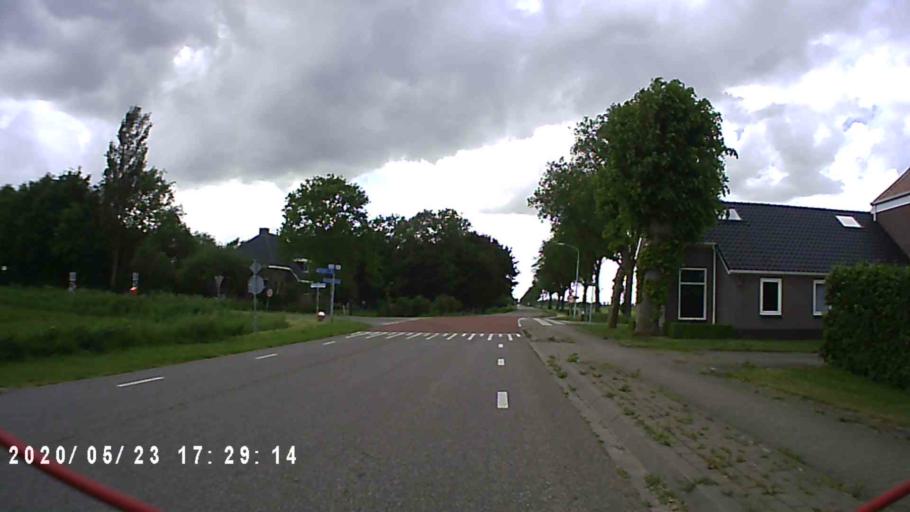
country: NL
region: Groningen
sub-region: Gemeente Slochteren
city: Slochteren
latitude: 53.2597
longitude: 6.7784
